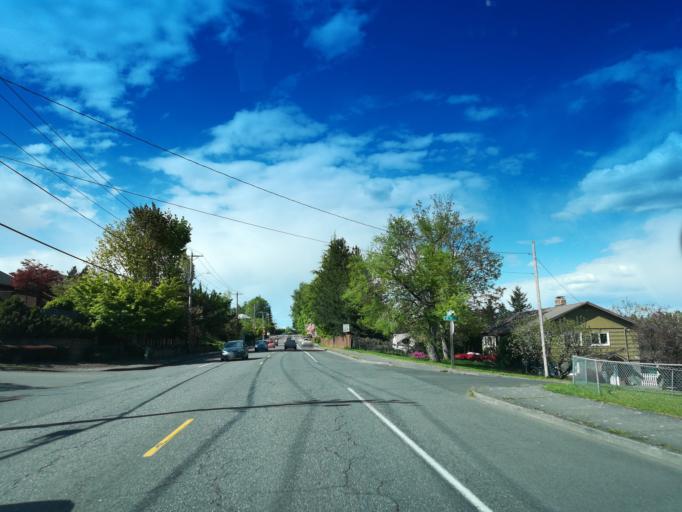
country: US
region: Oregon
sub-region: Multnomah County
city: Troutdale
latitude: 45.5290
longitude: -122.3874
